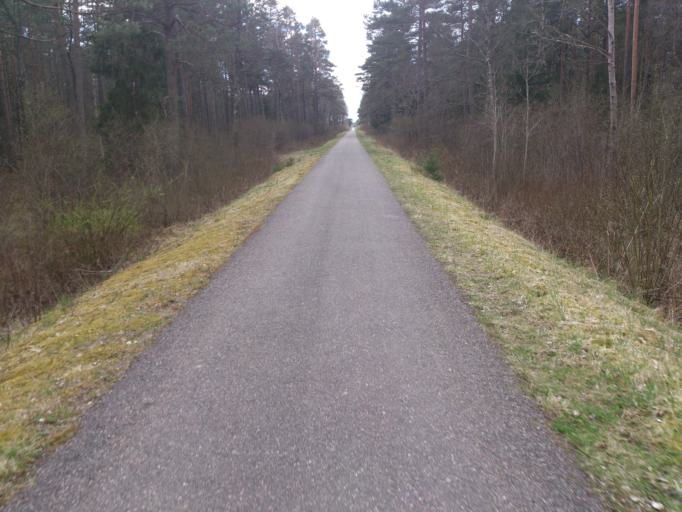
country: SE
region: Vaestra Goetaland
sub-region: Falkopings Kommun
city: Falkoeping
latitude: 57.9755
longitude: 13.5212
